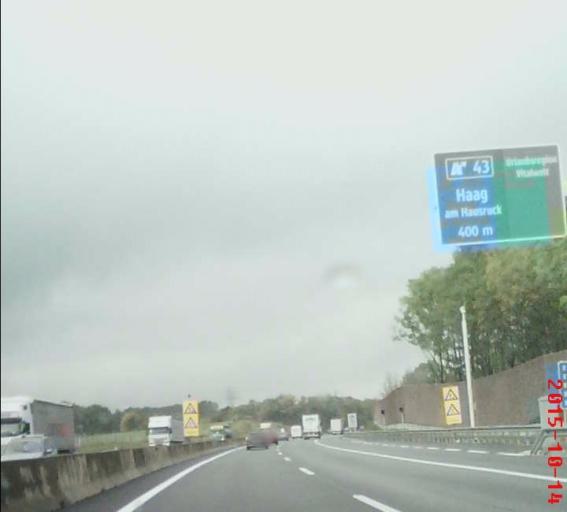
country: AT
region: Upper Austria
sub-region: Politischer Bezirk Vocklabruck
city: Wolfsegg am Hausruck
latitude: 48.1925
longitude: 13.6501
